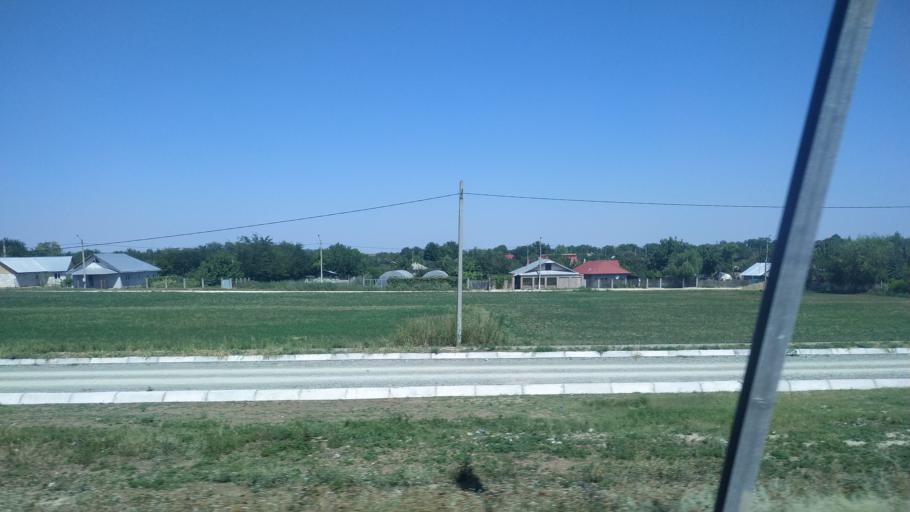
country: RO
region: Calarasi
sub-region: Comuna Perisoru
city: Perisoru
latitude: 44.4217
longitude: 27.6277
